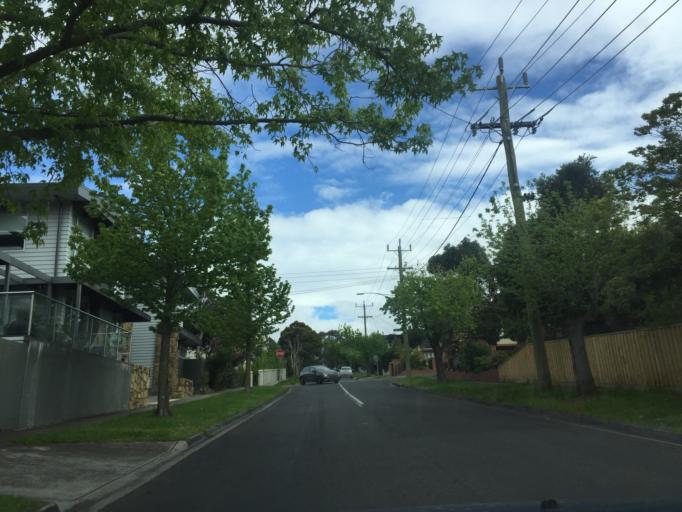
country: AU
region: Victoria
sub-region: Boroondara
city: Kew East
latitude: -37.8009
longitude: 145.0594
